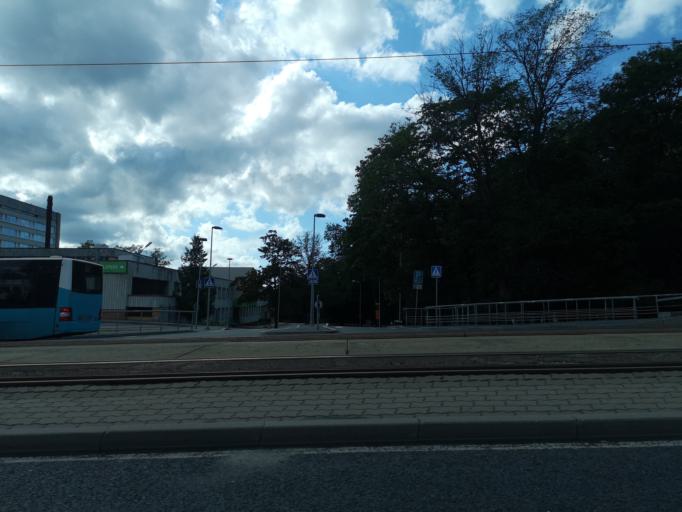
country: EE
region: Harju
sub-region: Tallinna linn
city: Tallinn
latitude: 59.4171
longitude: 24.7408
